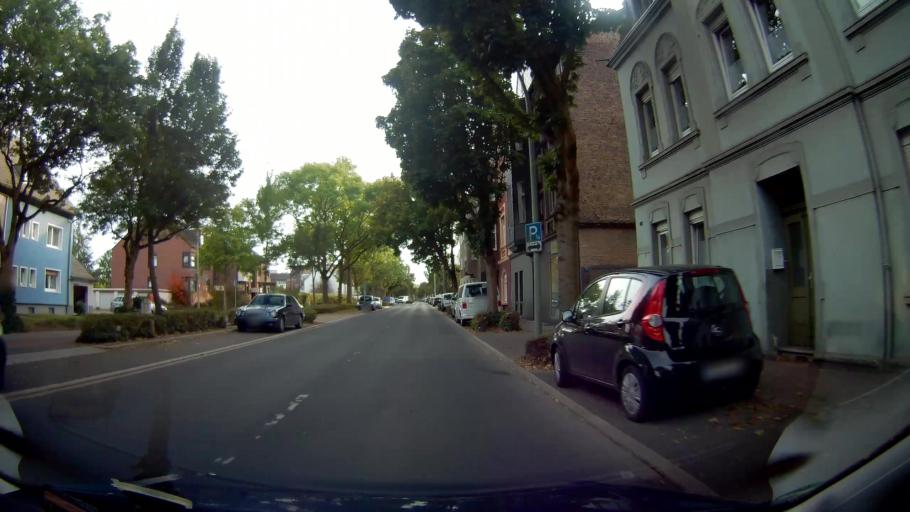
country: DE
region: North Rhine-Westphalia
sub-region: Regierungsbezirk Arnsberg
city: Herne
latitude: 51.5468
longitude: 7.2615
